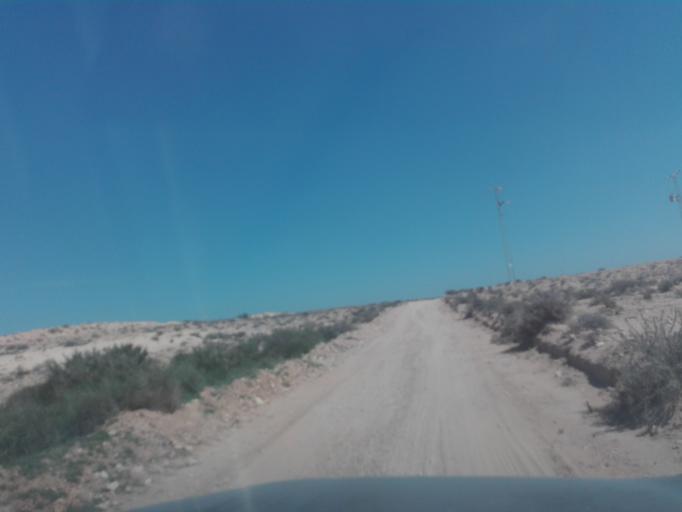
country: TN
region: Qabis
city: Gabes
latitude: 33.8458
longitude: 9.9902
